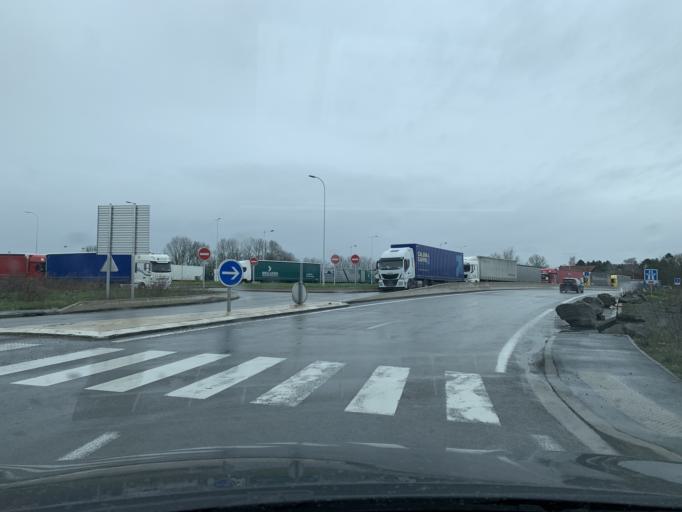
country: FR
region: Nord-Pas-de-Calais
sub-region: Departement du Nord
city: La Sentinelle
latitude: 50.3387
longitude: 3.4706
